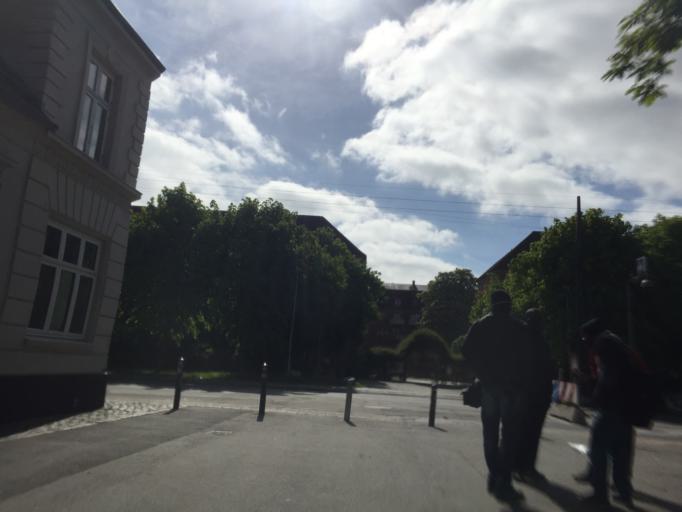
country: DK
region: Capital Region
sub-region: Kobenhavn
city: Copenhagen
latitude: 55.6877
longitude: 12.5551
